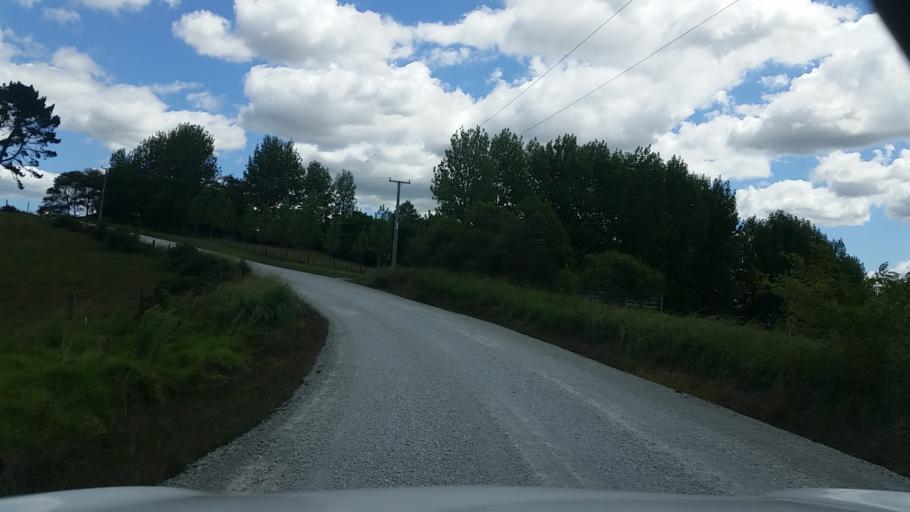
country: NZ
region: Northland
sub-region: Whangarei
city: Maungatapere
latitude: -35.6681
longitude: 174.1650
